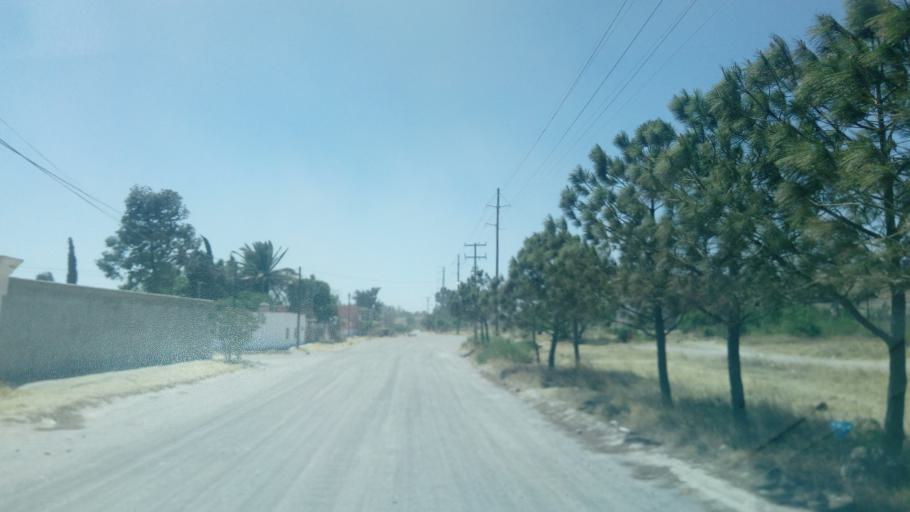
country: MX
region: Durango
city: Victoria de Durango
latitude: 24.0742
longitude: -104.6568
